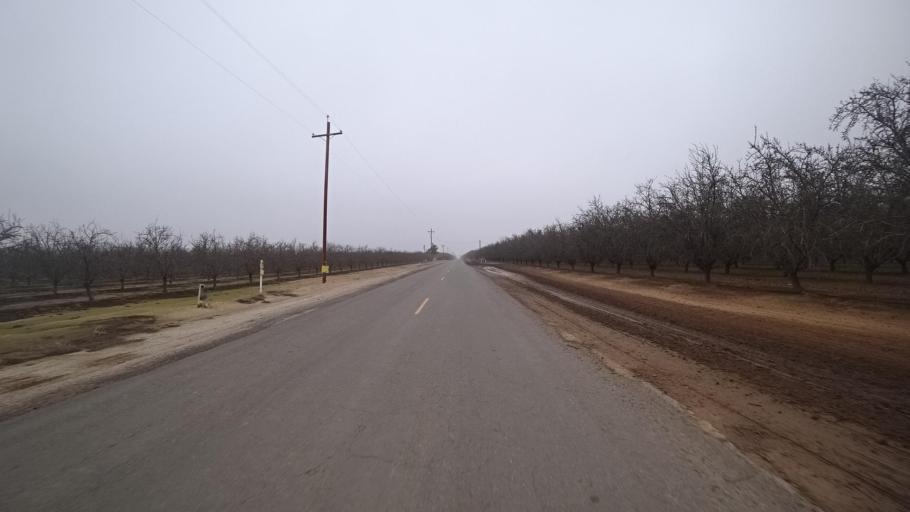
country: US
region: California
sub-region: Kern County
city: Wasco
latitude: 35.5773
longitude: -119.5095
